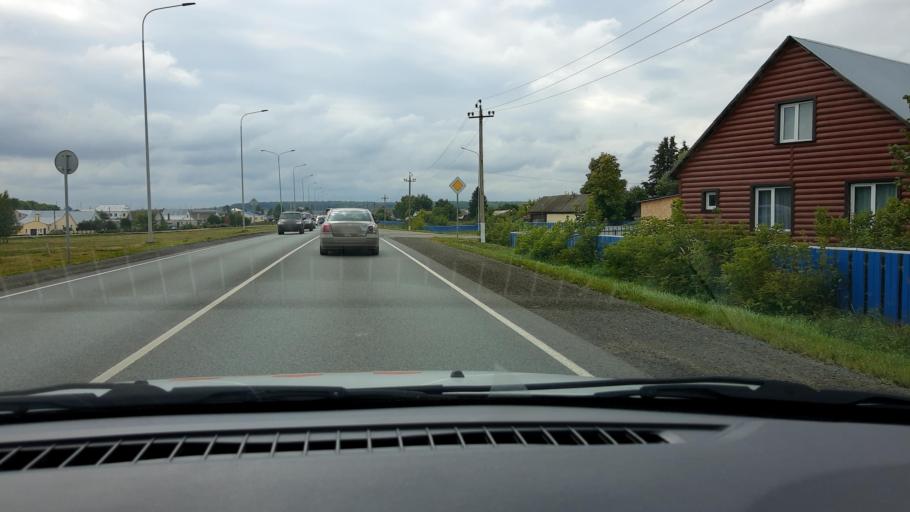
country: RU
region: Tatarstan
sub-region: Alekseyevskiy Rayon
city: Alekseyevskoye
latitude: 55.3020
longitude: 50.1303
